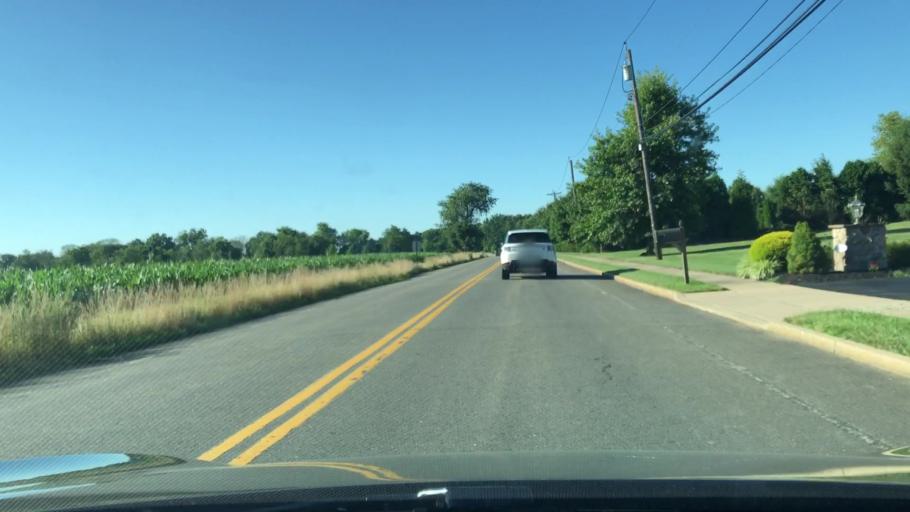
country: US
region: New Jersey
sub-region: Mercer County
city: Pennington
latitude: 40.3327
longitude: -74.8160
